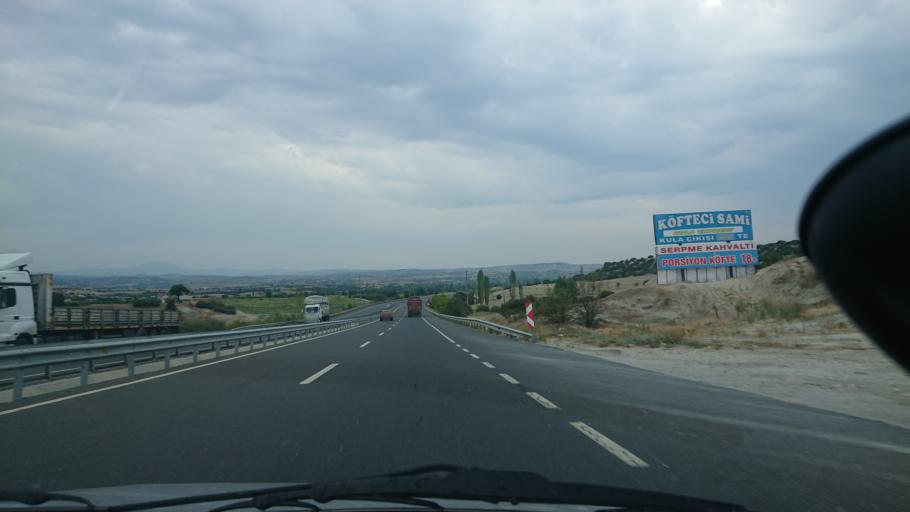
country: TR
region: Manisa
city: Selendi
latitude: 38.6261
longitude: 28.9301
